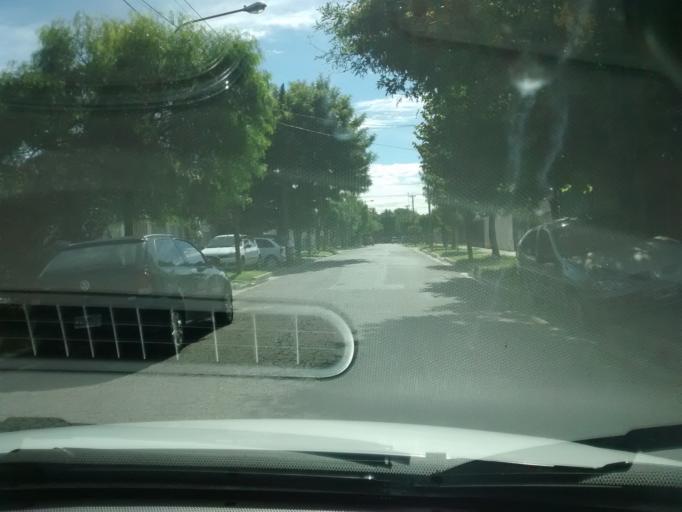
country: AR
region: Buenos Aires
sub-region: Partido de Moron
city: Moron
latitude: -34.6671
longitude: -58.6116
